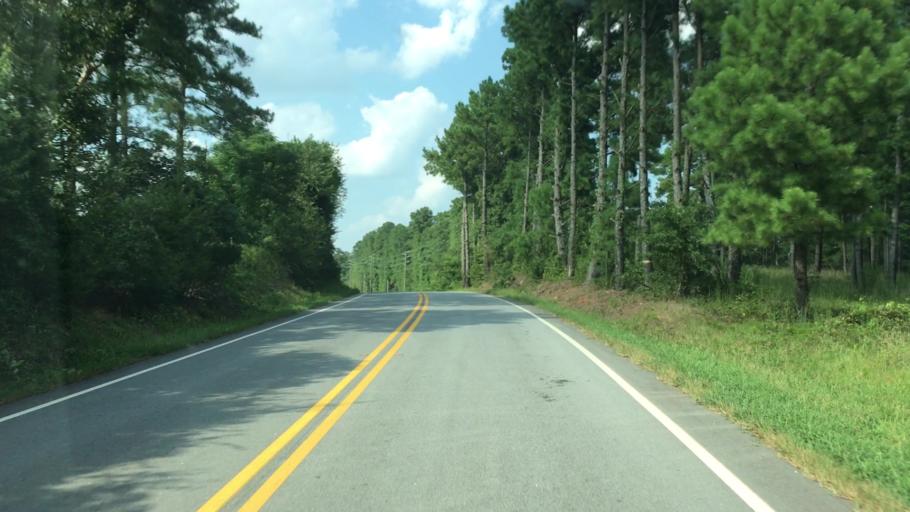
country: US
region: Georgia
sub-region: Jasper County
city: Monticello
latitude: 33.4546
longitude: -83.7533
